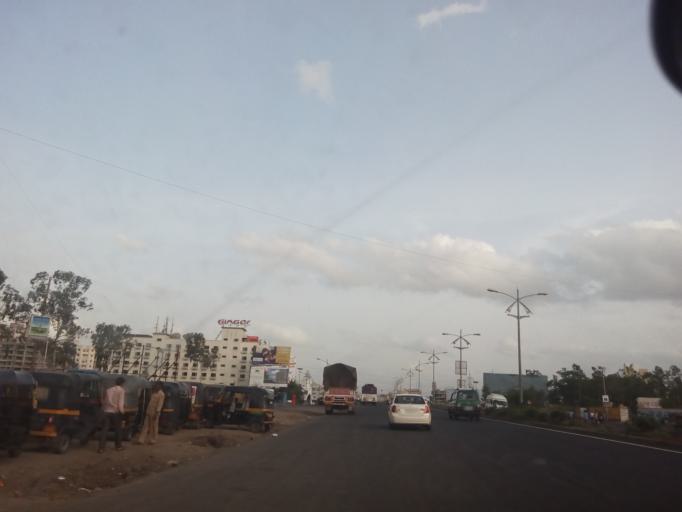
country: IN
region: Maharashtra
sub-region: Pune Division
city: Pimpri
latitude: 18.6082
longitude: 73.7512
